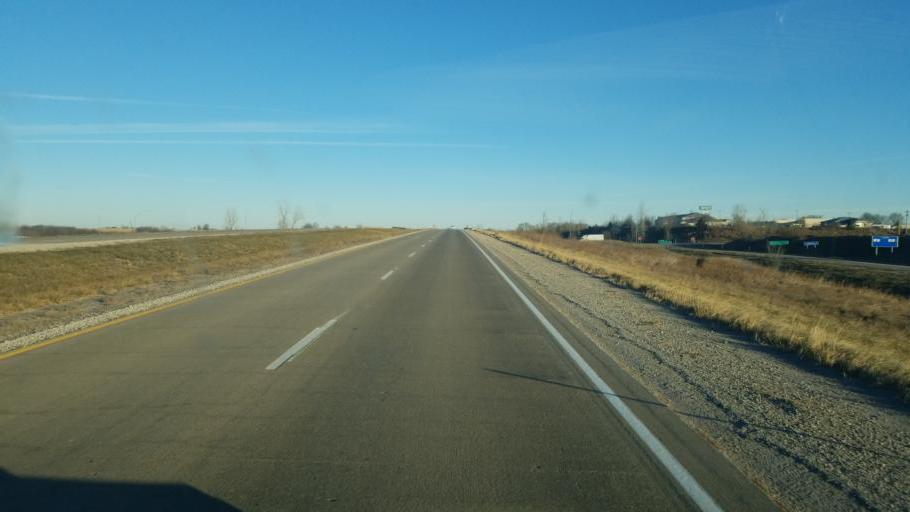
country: US
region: Iowa
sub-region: Mahaska County
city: Oskaloosa
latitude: 41.2934
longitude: -92.6745
